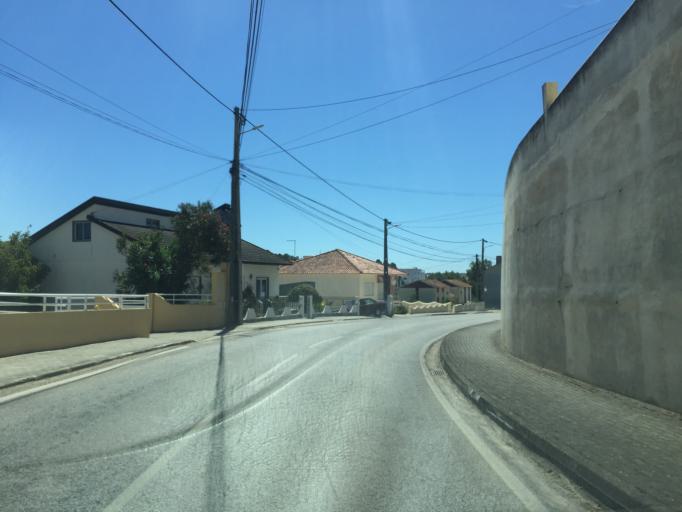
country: PT
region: Lisbon
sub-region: Torres Vedras
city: A dos Cunhados
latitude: 39.1796
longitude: -9.3227
